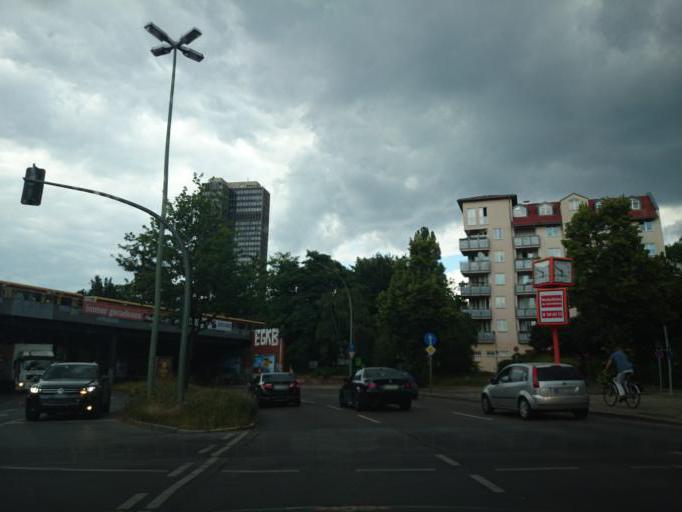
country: DE
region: Berlin
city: Steglitz Bezirk
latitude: 52.4526
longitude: 13.3197
